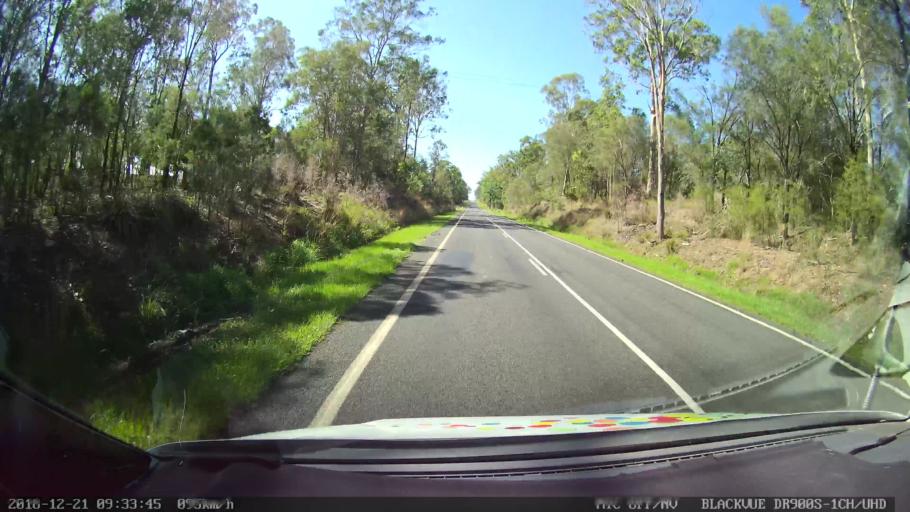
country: AU
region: New South Wales
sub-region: Clarence Valley
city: Grafton
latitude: -29.4888
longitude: 152.9770
